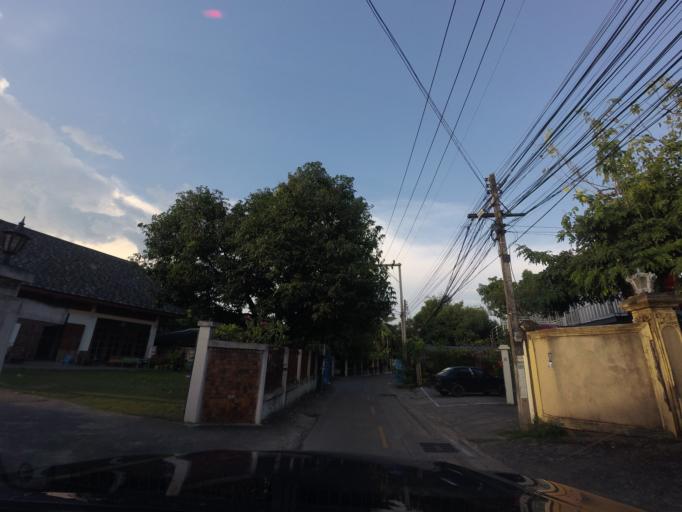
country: TH
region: Khon Kaen
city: Khon Kaen
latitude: 16.4329
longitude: 102.8568
